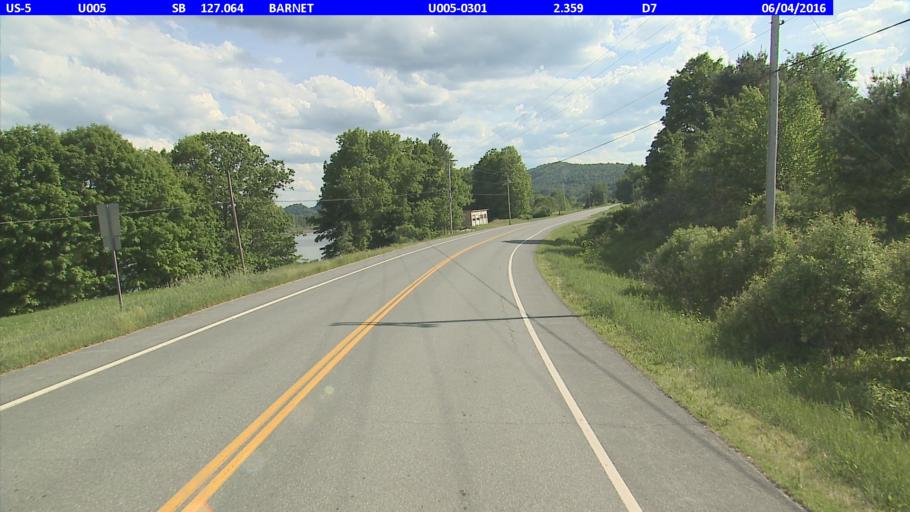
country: US
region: New Hampshire
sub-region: Grafton County
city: Woodsville
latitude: 44.2870
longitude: -72.0595
